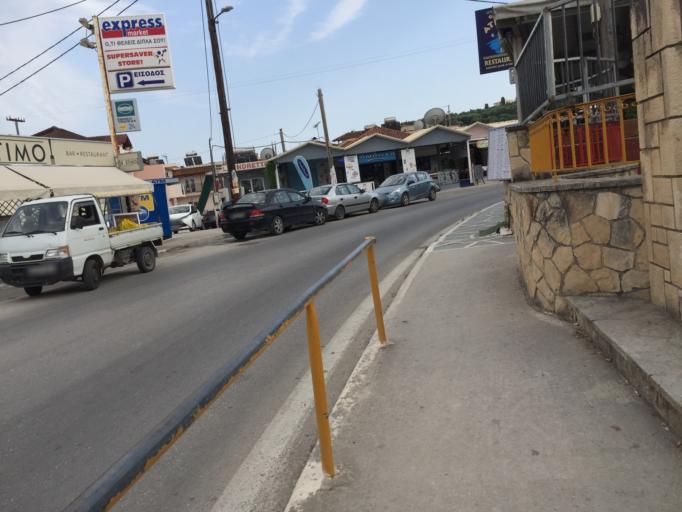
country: GR
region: Ionian Islands
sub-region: Nomos Zakynthou
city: Gaitanion
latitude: 37.8117
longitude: 20.8723
